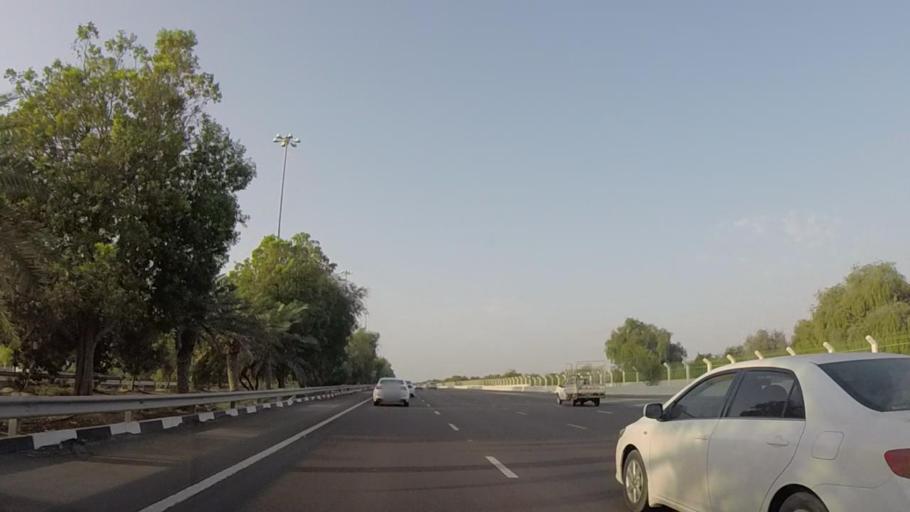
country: AE
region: Dubai
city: Dubai
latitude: 24.8591
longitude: 54.9052
